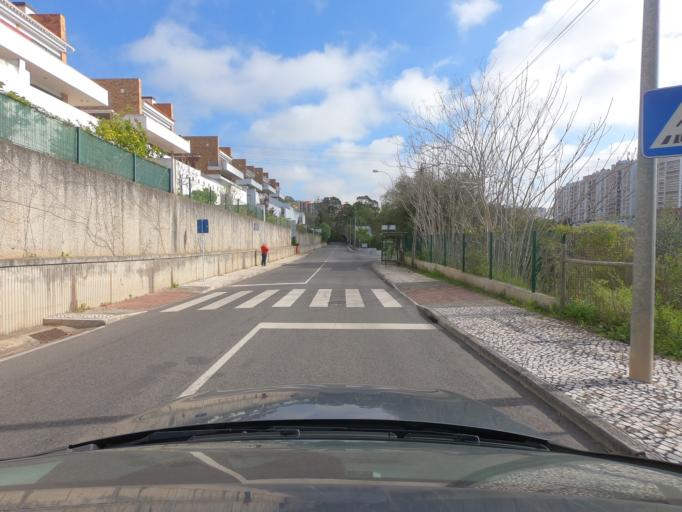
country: PT
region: Lisbon
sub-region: Oeiras
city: Carnaxide
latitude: 38.7205
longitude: -9.2509
